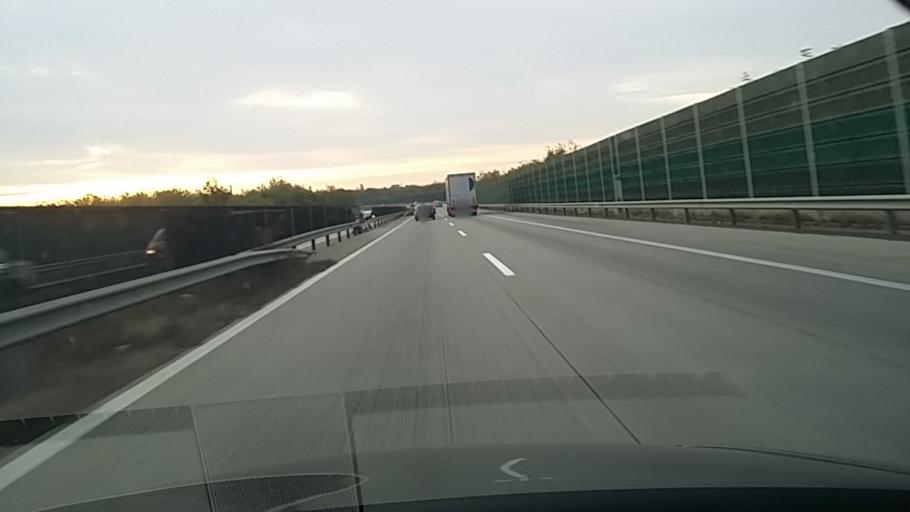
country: HU
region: Pest
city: Csomor
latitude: 47.5344
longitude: 19.2219
